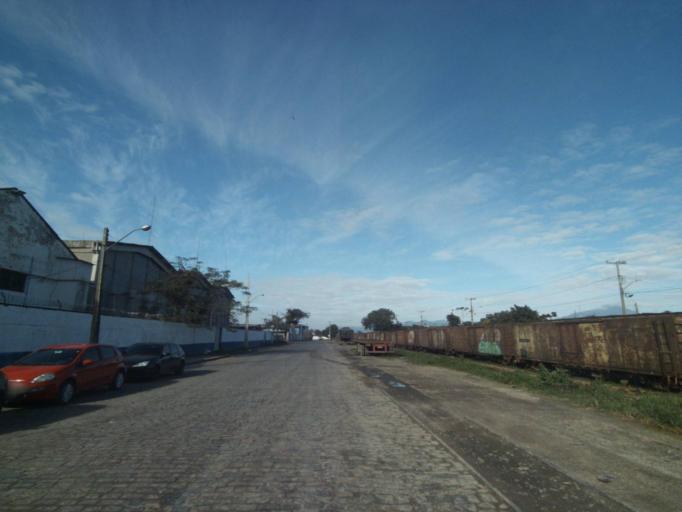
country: BR
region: Parana
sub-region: Paranagua
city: Paranagua
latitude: -25.5225
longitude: -48.5279
